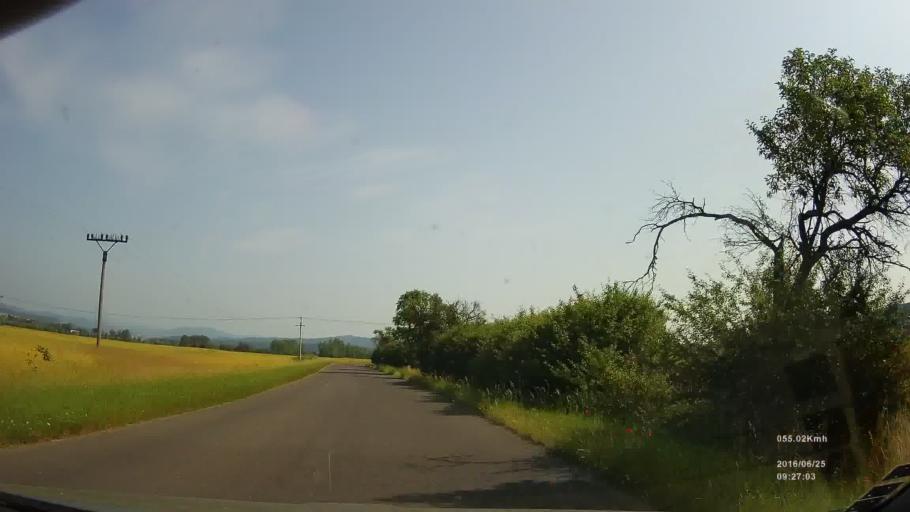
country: SK
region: Banskobystricky
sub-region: Okres Banska Bystrica
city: Zvolen
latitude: 48.6182
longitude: 19.1476
